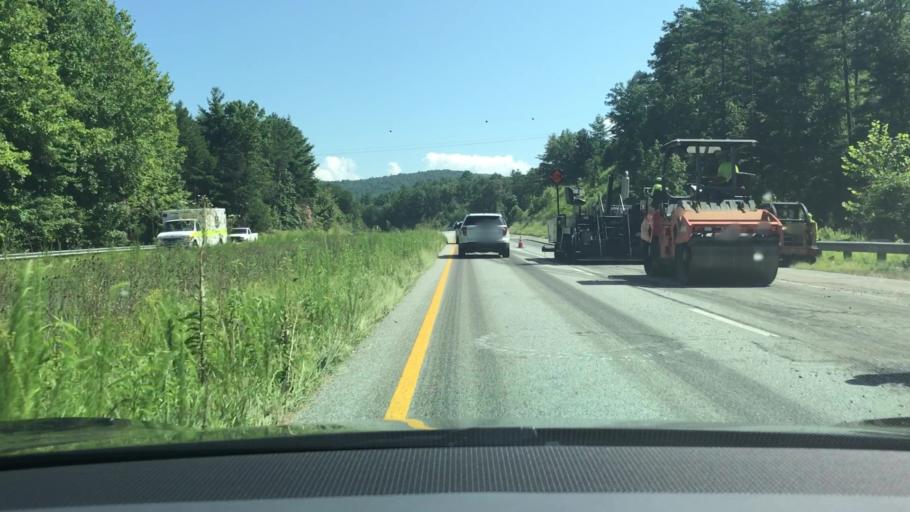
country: US
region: Georgia
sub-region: Rabun County
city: Clayton
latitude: 34.7505
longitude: -83.3994
